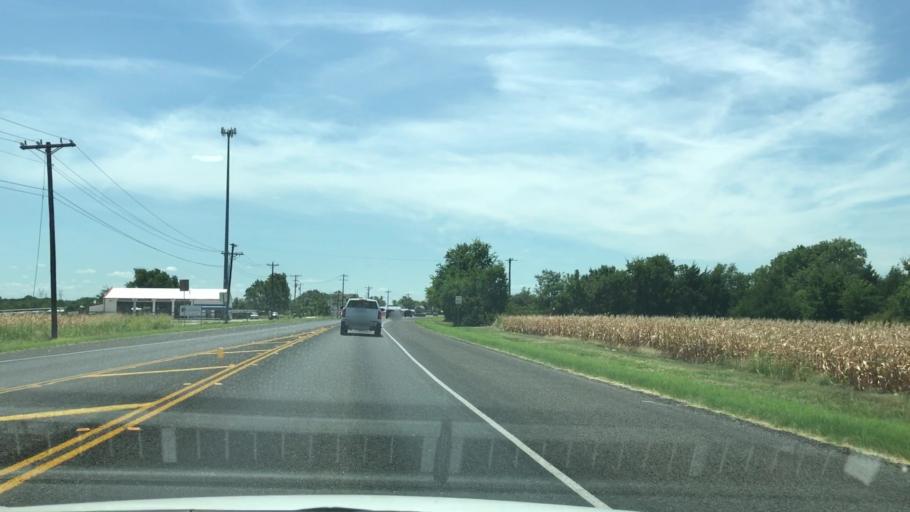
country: US
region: Texas
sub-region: Collin County
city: Lavon
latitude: 33.0172
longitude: -96.4566
